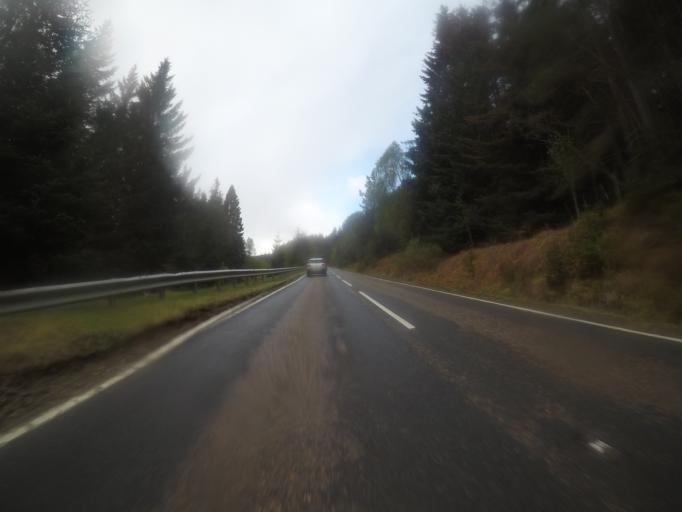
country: GB
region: Scotland
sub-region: Highland
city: Spean Bridge
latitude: 57.0829
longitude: -4.9288
